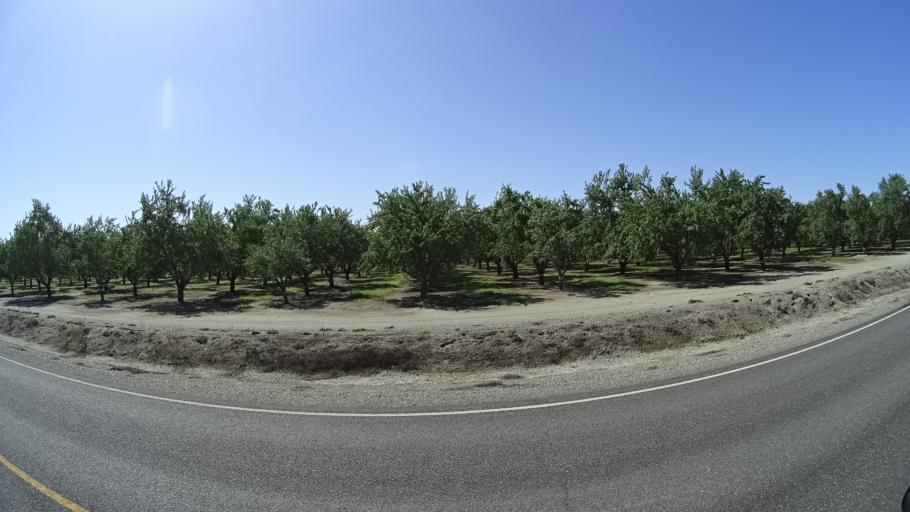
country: US
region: California
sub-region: Glenn County
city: Hamilton City
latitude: 39.7106
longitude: -122.0923
